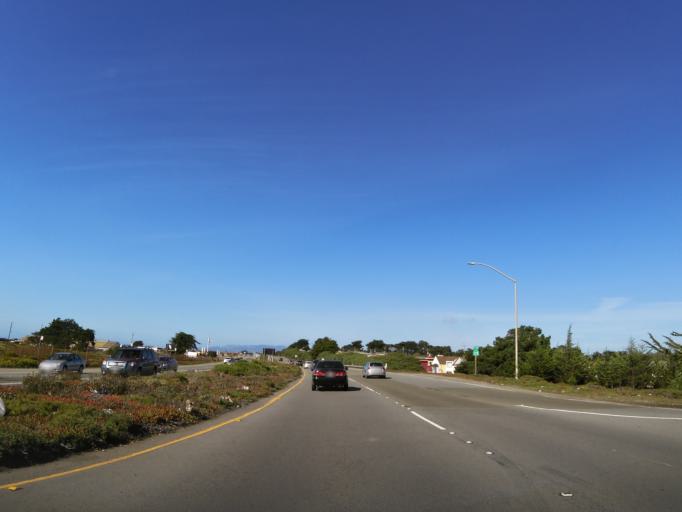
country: US
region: California
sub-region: San Mateo County
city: Broadmoor
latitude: 37.6986
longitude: -122.4949
